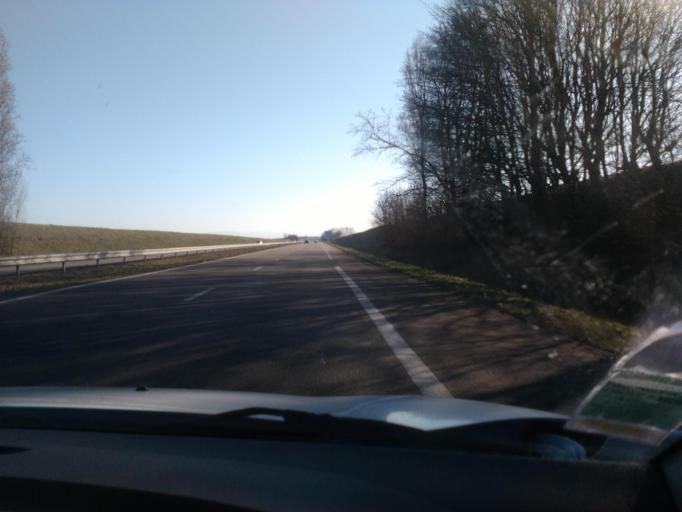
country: FR
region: Alsace
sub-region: Departement du Bas-Rhin
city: Altorf
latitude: 48.5147
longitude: 7.5432
